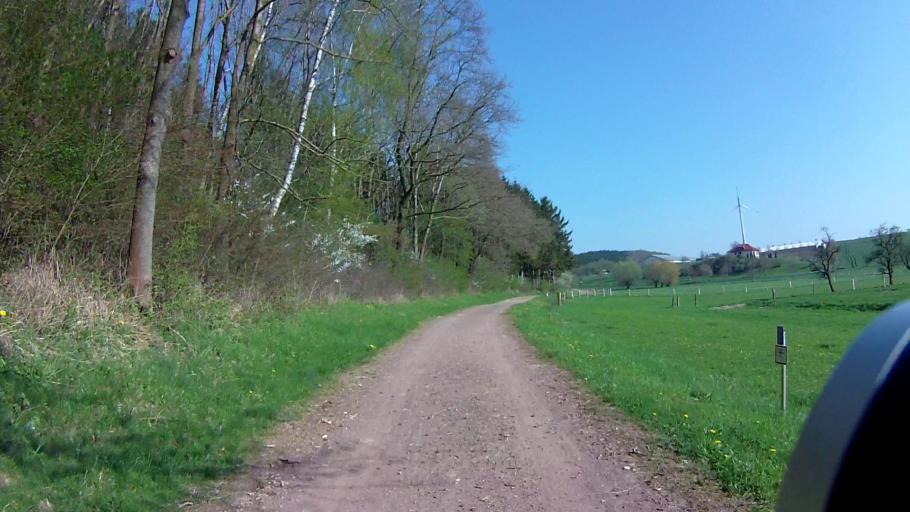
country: DE
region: North Rhine-Westphalia
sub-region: Regierungsbezirk Detmold
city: Paderborn
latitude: 51.6971
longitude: 8.8277
